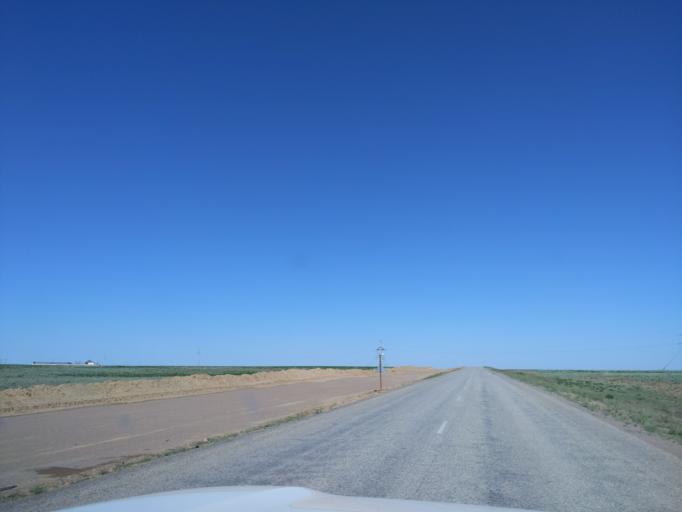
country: KZ
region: Almaty Oblysy
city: Bakanas
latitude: 44.1841
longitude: 75.7949
